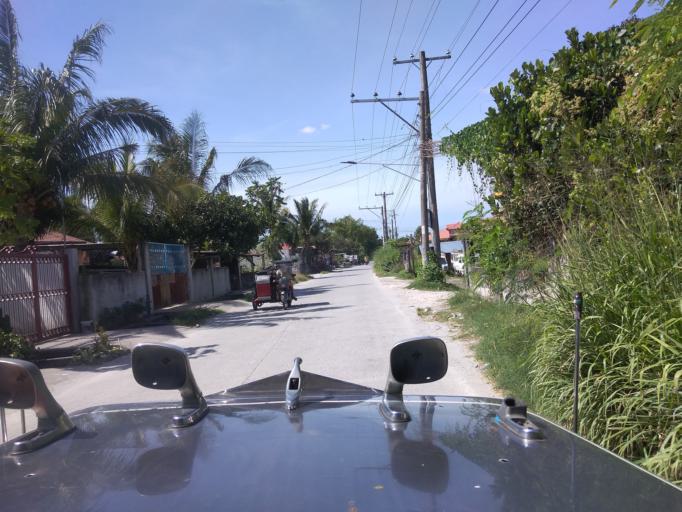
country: PH
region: Central Luzon
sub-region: Province of Pampanga
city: Magliman
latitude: 15.0189
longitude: 120.6577
